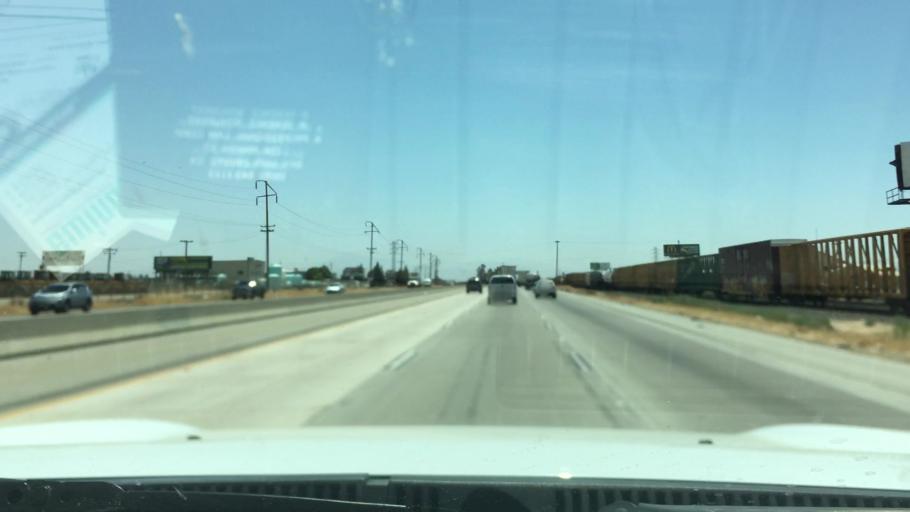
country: US
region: California
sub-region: Kern County
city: Greenacres
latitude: 35.4492
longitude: -119.0977
